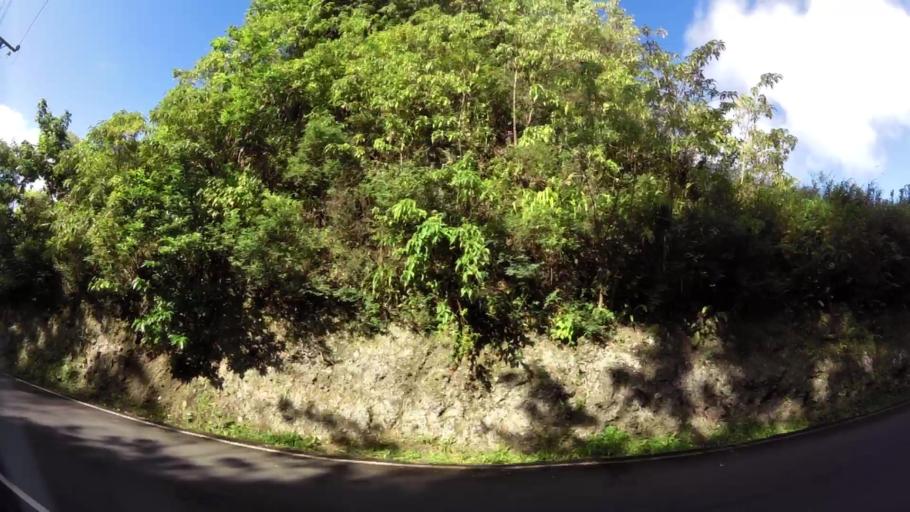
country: LC
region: Soufriere
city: Soufriere
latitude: 13.8684
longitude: -61.0490
